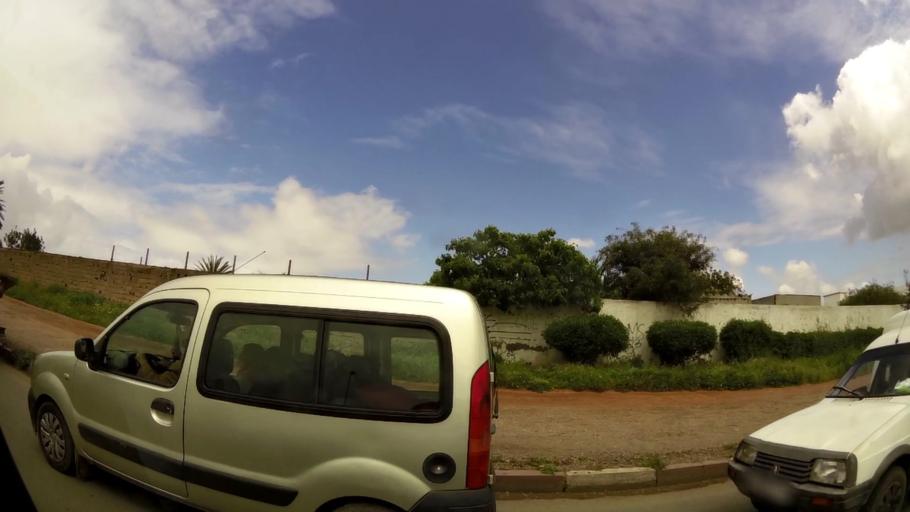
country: MA
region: Grand Casablanca
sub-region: Mediouna
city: Tit Mellil
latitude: 33.6059
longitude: -7.4941
